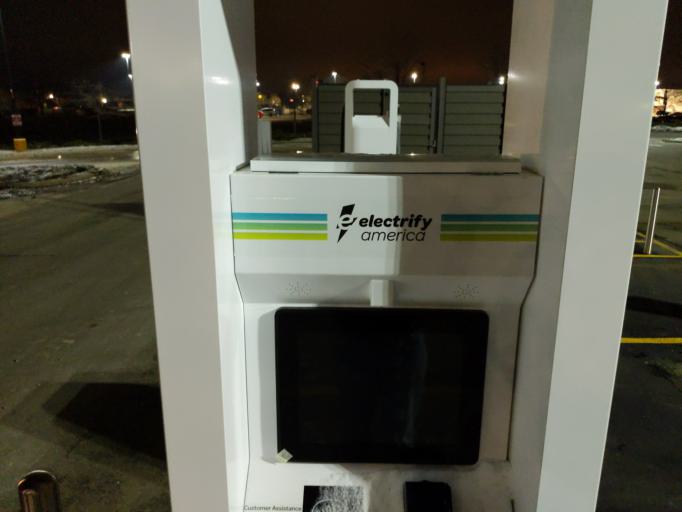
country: US
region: Michigan
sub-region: Eaton County
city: Waverly
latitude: 42.7393
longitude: -84.6738
